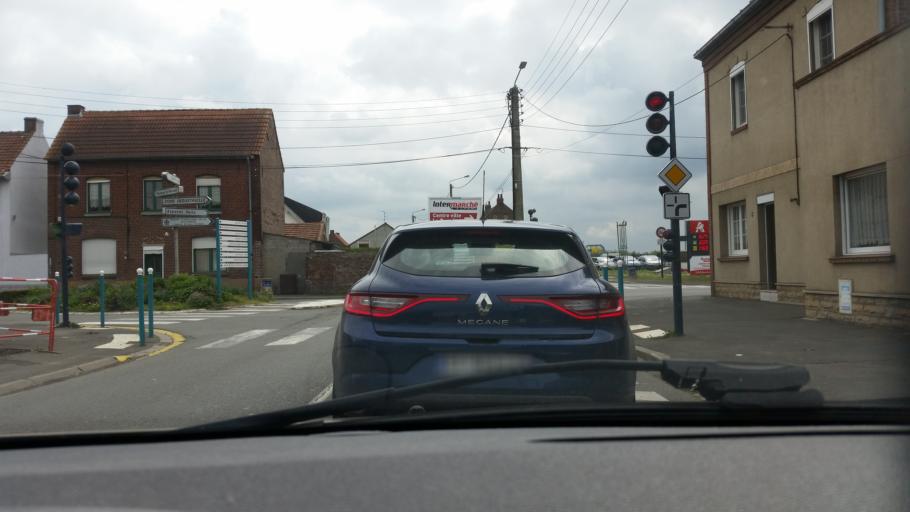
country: FR
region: Nord-Pas-de-Calais
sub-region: Departement du Pas-de-Calais
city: Billy-Berclau
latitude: 50.5121
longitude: 2.8568
